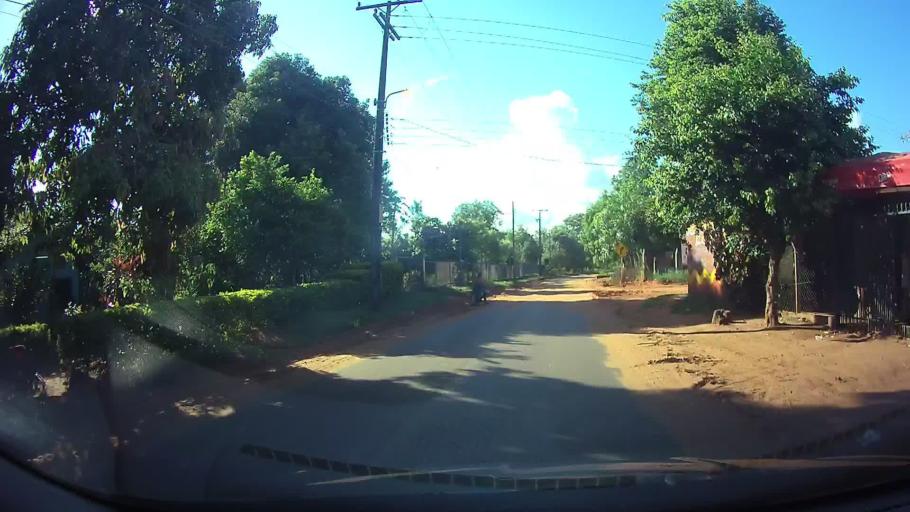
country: PY
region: Central
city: Itaugua
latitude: -25.3680
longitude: -57.3698
